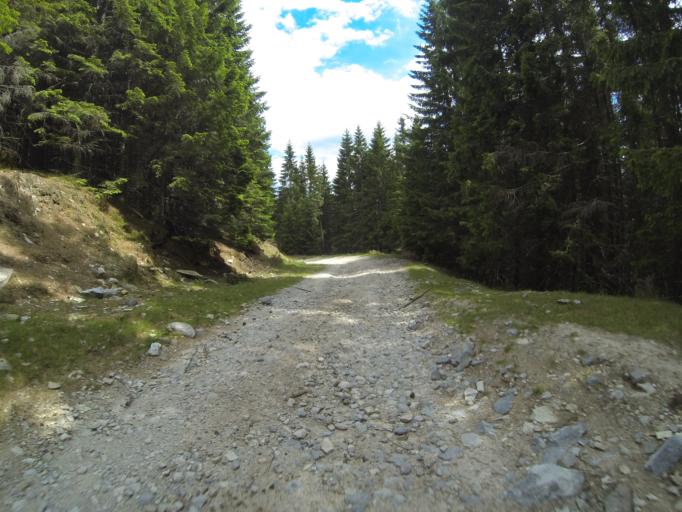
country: RO
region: Gorj
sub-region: Comuna Polovragi
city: Polovragi
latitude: 45.3426
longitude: 23.7935
